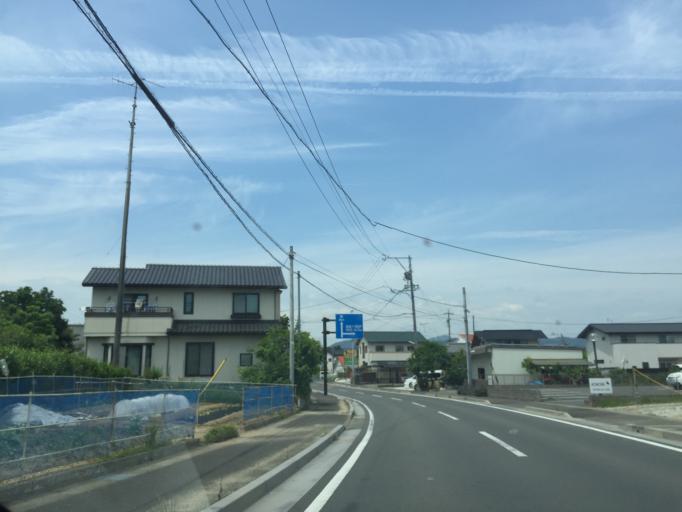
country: JP
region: Shizuoka
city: Kakegawa
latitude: 34.7910
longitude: 138.0086
